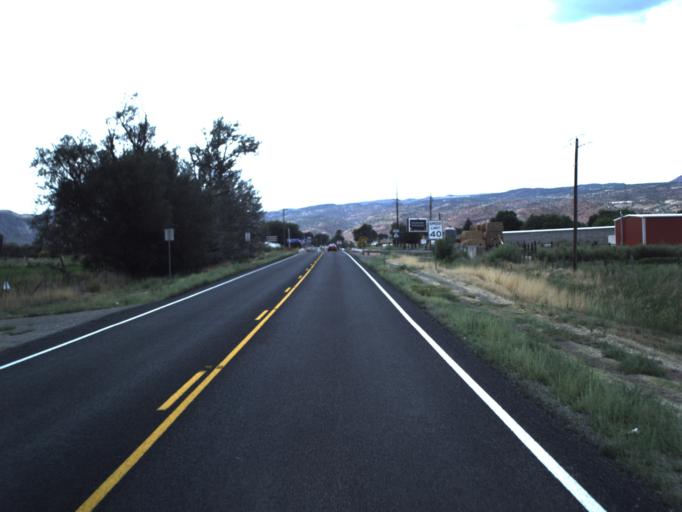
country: US
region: Utah
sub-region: Sevier County
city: Richfield
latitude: 38.7725
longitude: -112.0653
